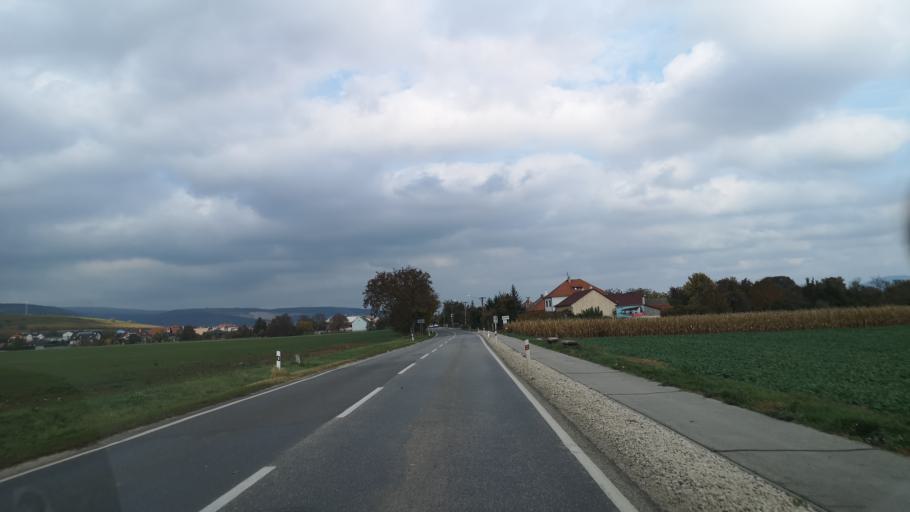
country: SK
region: Nitriansky
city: Cachtice
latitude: 48.6839
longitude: 17.7773
